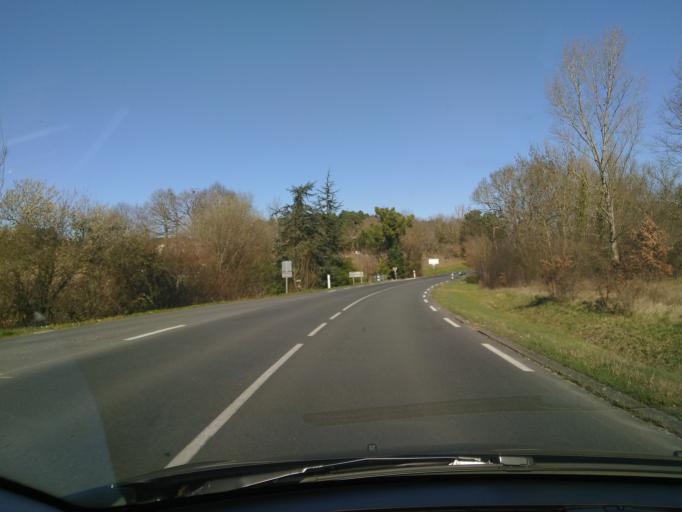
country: FR
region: Aquitaine
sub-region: Departement de la Dordogne
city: Monbazillac
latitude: 44.7867
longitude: 0.5241
